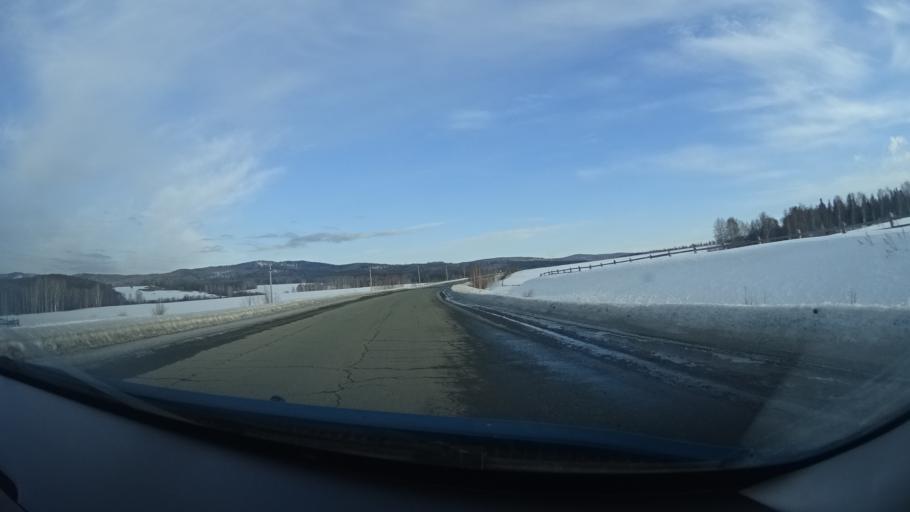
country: RU
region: Bashkortostan
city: Lomovka
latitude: 53.7216
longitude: 58.2505
